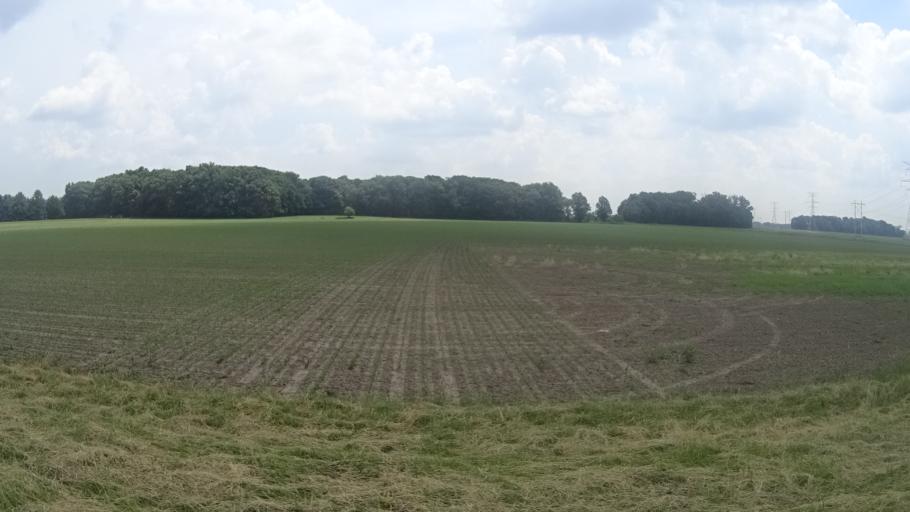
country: US
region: Ohio
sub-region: Erie County
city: Milan
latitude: 41.3398
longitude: -82.6722
